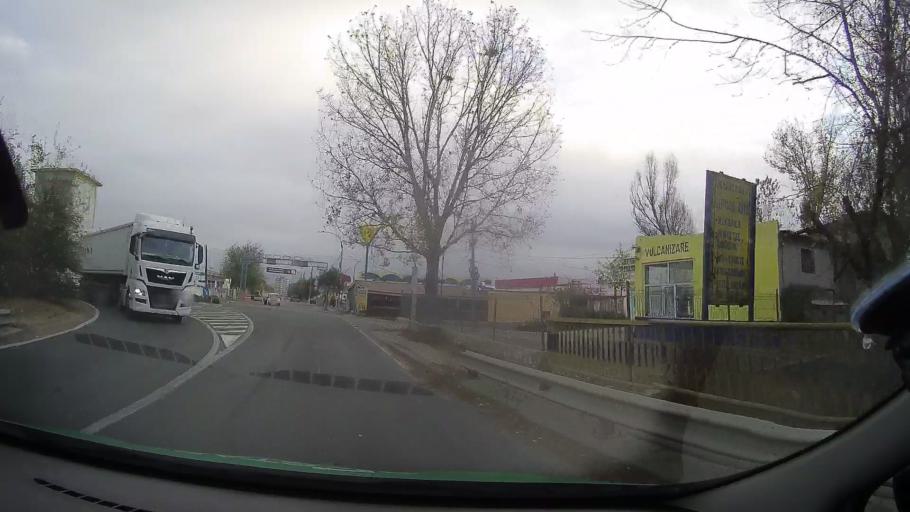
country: RO
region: Constanta
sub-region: Municipiul Medgidia
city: Medgidia
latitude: 44.2667
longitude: 28.2574
